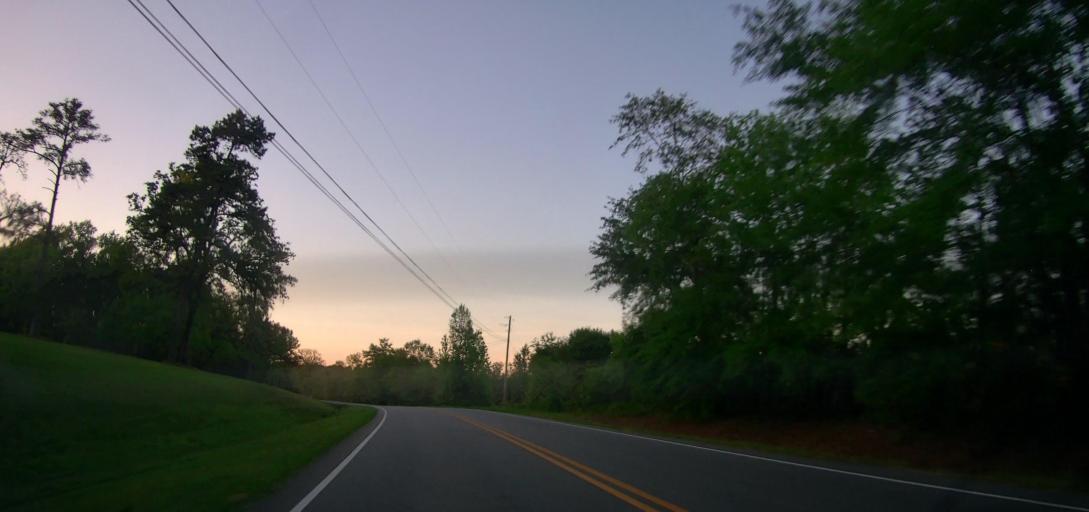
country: US
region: Georgia
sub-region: Marion County
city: Buena Vista
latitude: 32.3473
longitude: -84.5324
